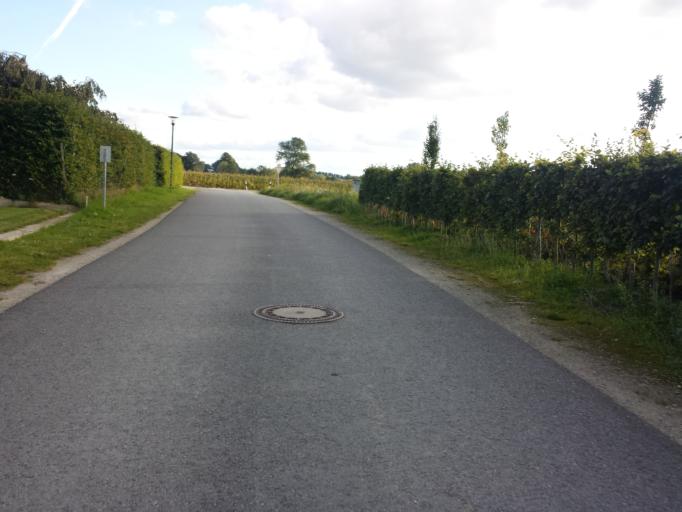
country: DE
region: North Rhine-Westphalia
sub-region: Regierungsbezirk Detmold
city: Langenberg
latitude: 51.7452
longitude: 8.3205
